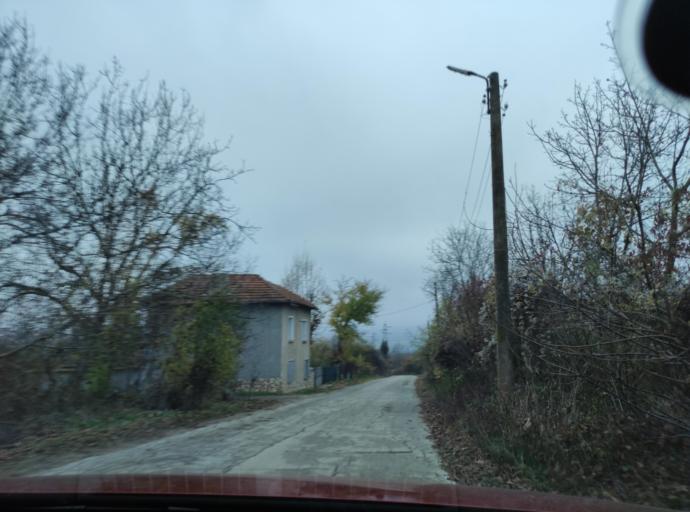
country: BG
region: Lovech
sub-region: Obshtina Yablanitsa
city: Yablanitsa
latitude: 43.0979
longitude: 24.0748
